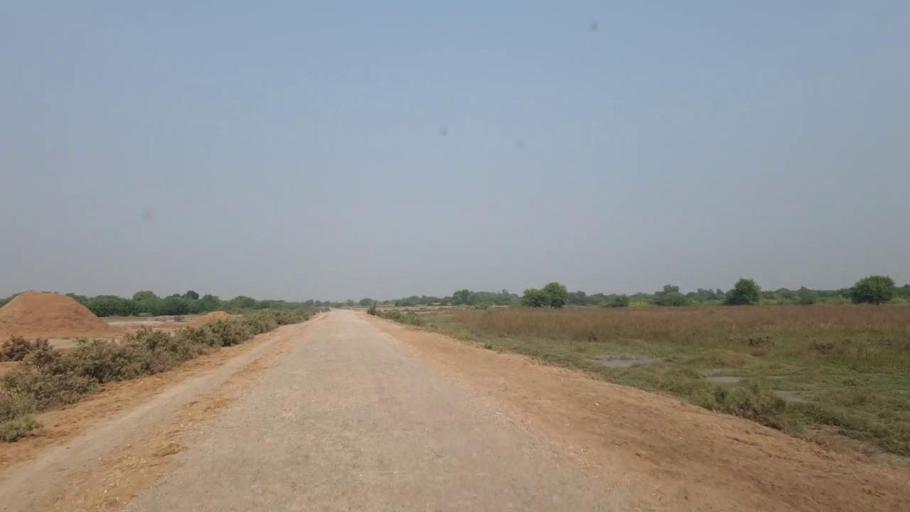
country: PK
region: Sindh
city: Matli
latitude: 25.1587
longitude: 68.7295
